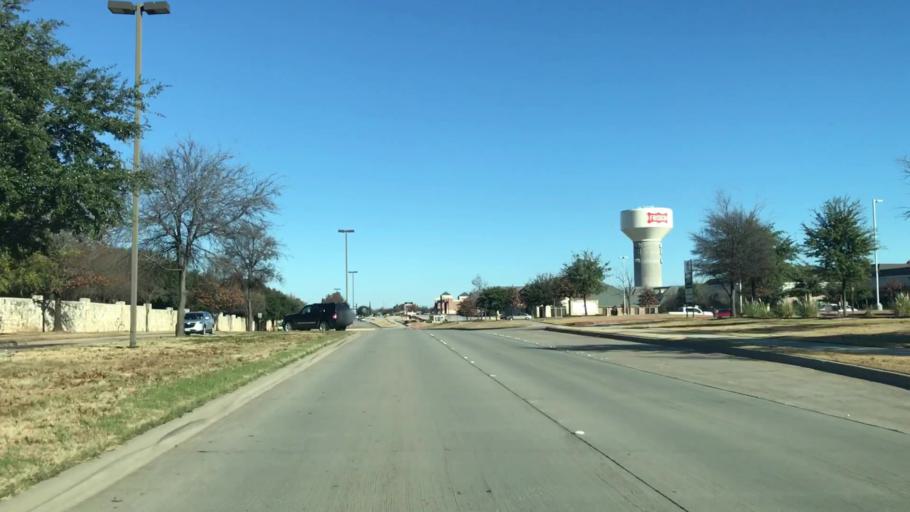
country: US
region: Texas
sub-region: Denton County
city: The Colony
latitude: 33.1017
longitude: -96.8417
